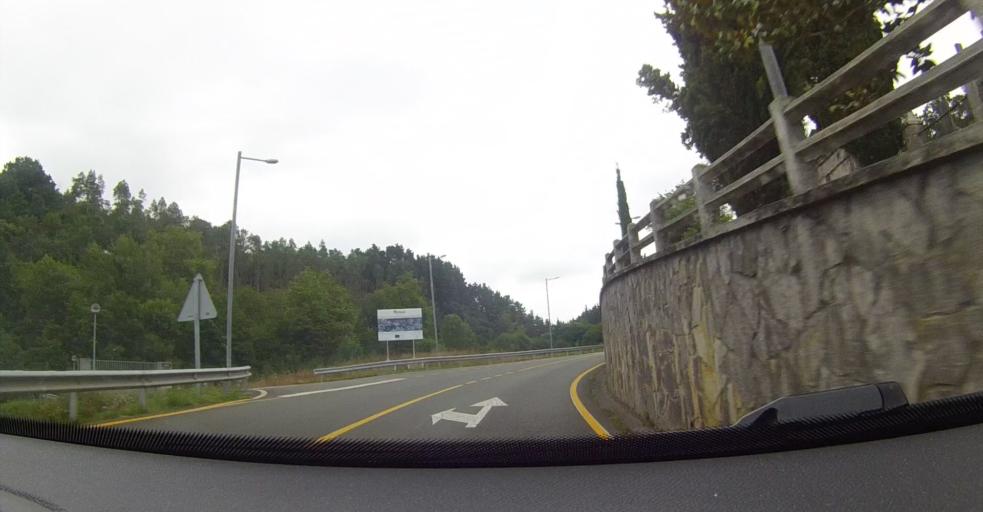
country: ES
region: Basque Country
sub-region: Bizkaia
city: Balmaseda
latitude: 43.2428
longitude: -3.2127
